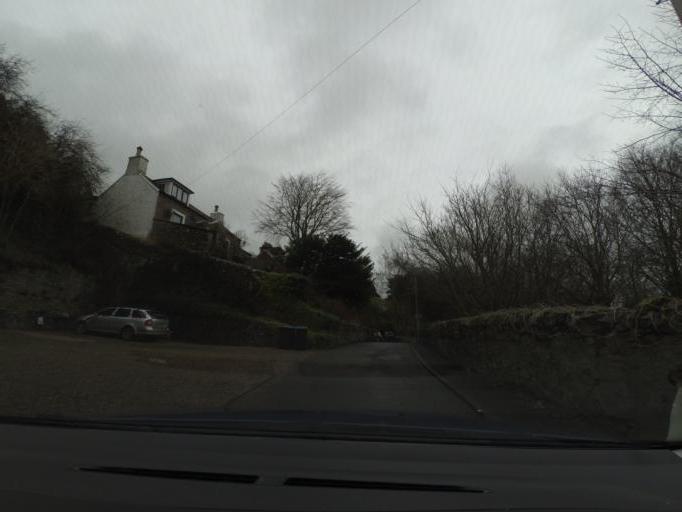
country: GB
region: Scotland
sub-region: The Scottish Borders
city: Hawick
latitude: 55.4231
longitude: -2.8057
